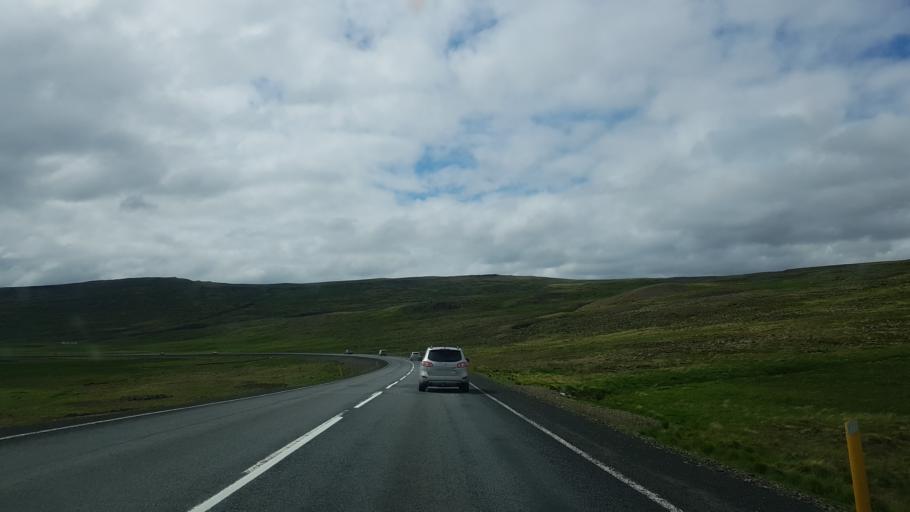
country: IS
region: West
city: Borgarnes
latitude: 64.9080
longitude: -21.1701
